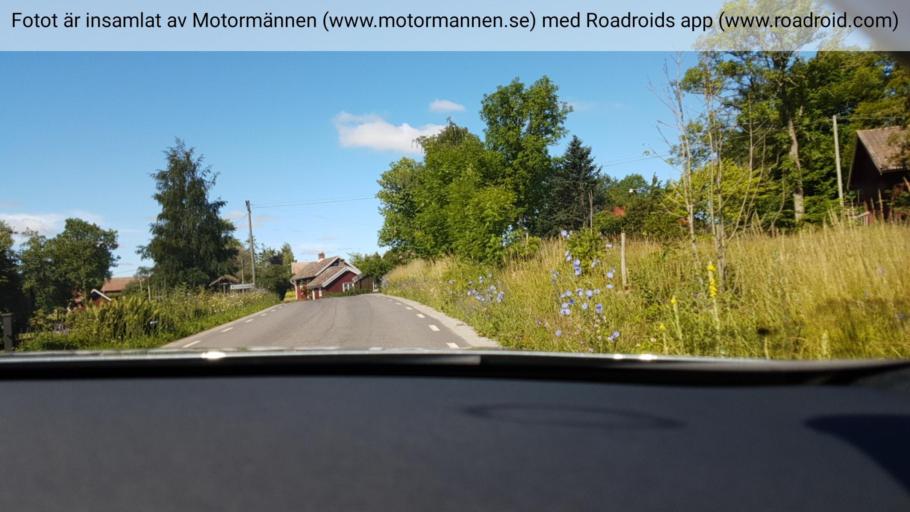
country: SE
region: Vaestra Goetaland
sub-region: Falkopings Kommun
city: Akarp
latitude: 58.2577
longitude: 13.6689
